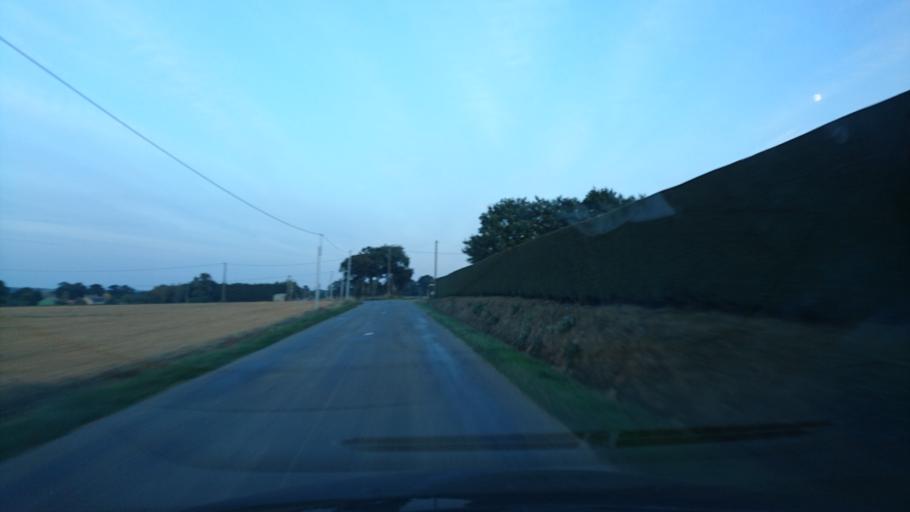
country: FR
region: Brittany
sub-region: Departement d'Ille-et-Vilaine
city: Guignen
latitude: 47.9115
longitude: -1.9023
